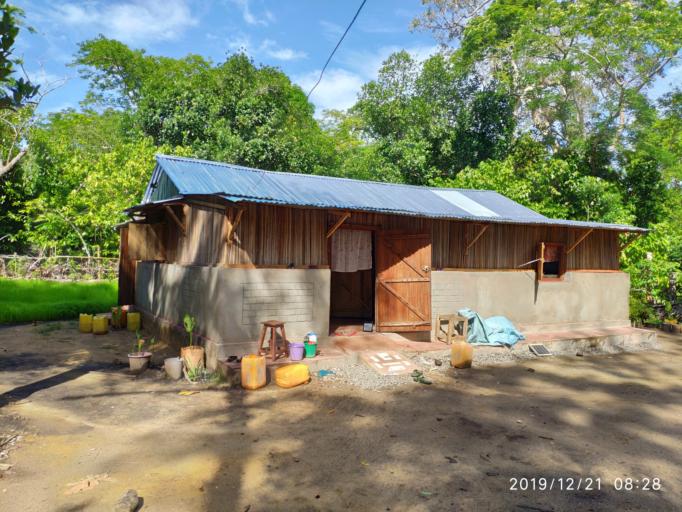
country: MG
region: Diana
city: Ambanja
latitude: -13.6292
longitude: 48.4565
